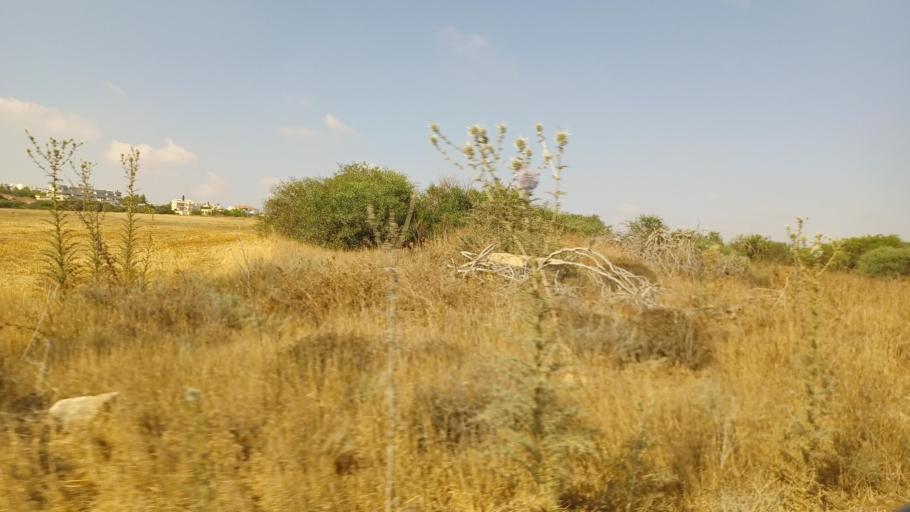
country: CY
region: Ammochostos
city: Deryneia
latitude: 35.0680
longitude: 33.9724
